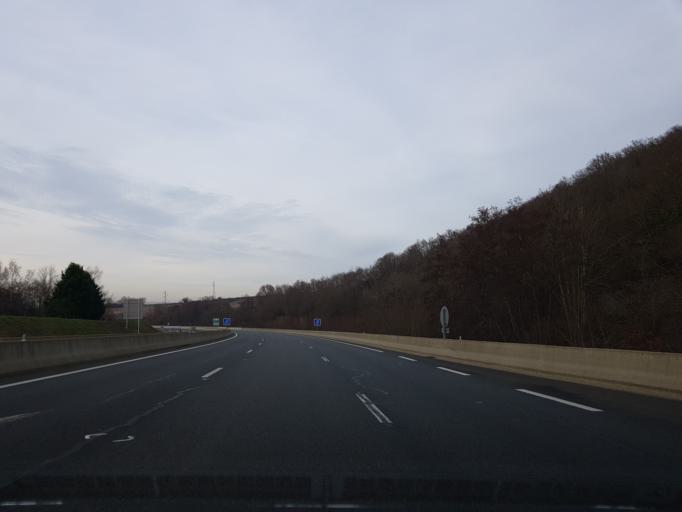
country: FR
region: Auvergne
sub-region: Departement de l'Allier
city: Desertines
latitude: 46.3745
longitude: 2.6296
